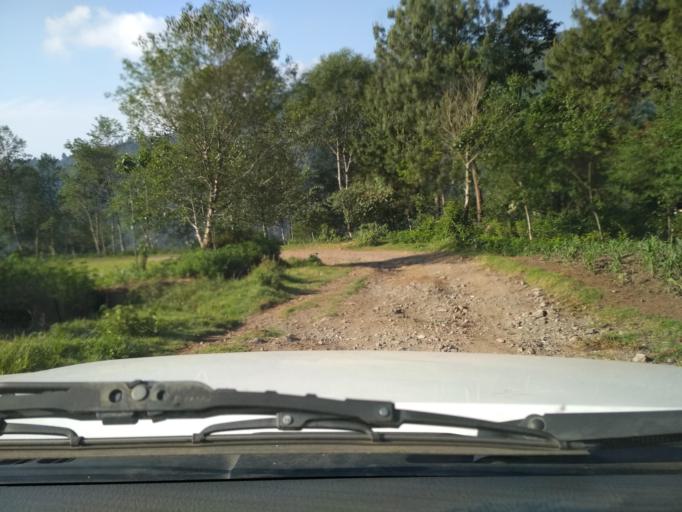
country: MX
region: Veracruz
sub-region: La Perla
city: Chilapa
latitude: 18.9862
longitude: -97.1674
